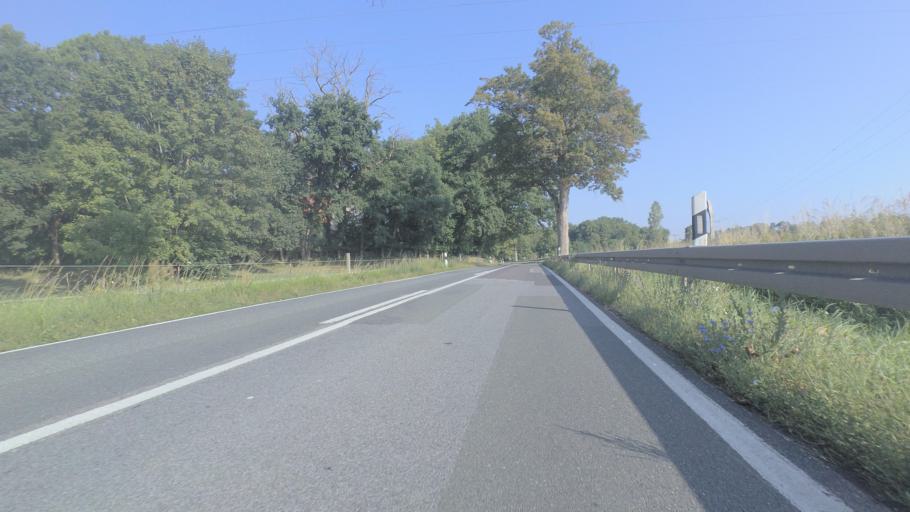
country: DE
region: Mecklenburg-Vorpommern
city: Malchow
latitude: 53.4449
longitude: 12.4329
